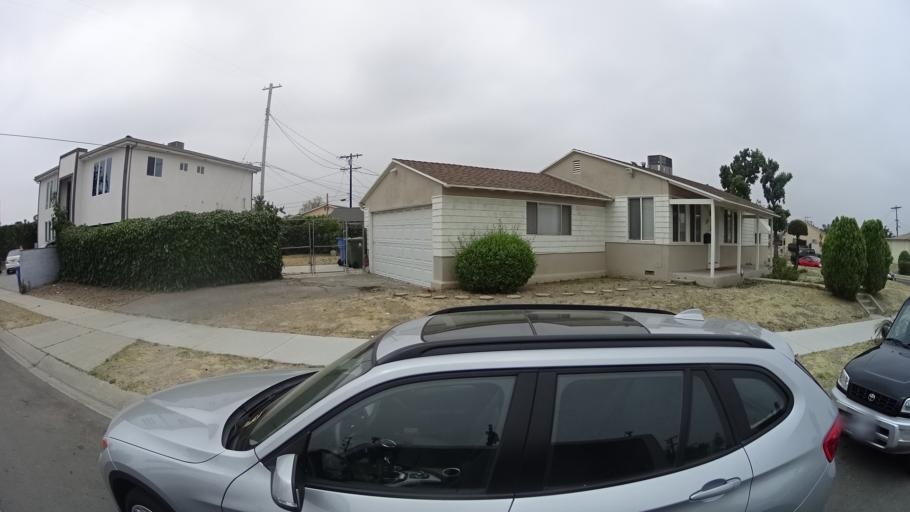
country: US
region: California
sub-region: Los Angeles County
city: North Hollywood
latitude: 34.1930
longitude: -118.4091
